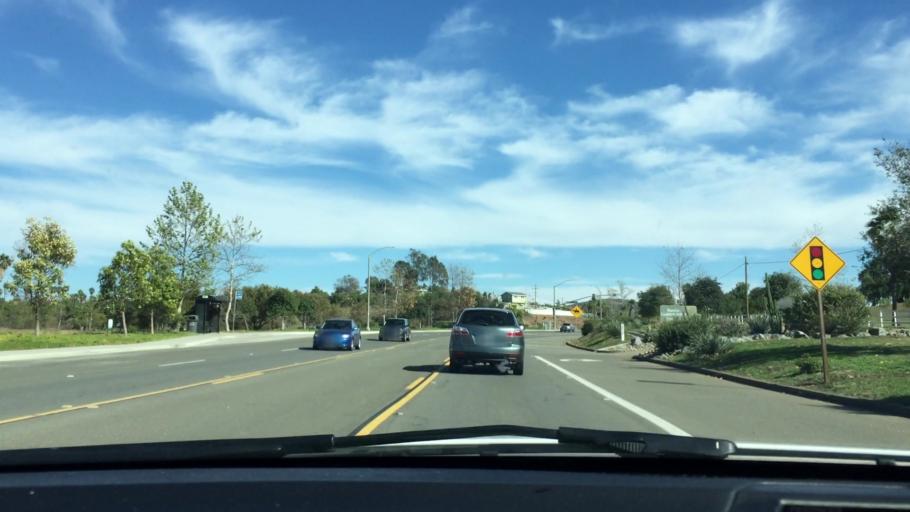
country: US
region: California
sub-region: San Diego County
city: Vista
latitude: 33.2346
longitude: -117.2533
